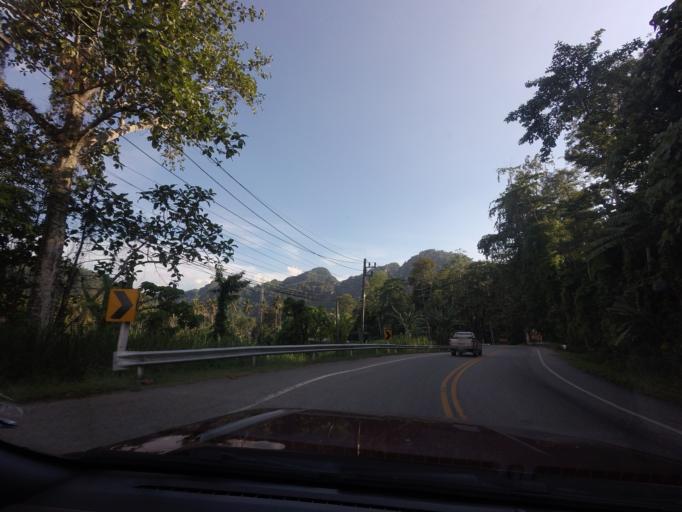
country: TH
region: Yala
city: Than To
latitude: 6.1996
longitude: 101.1742
